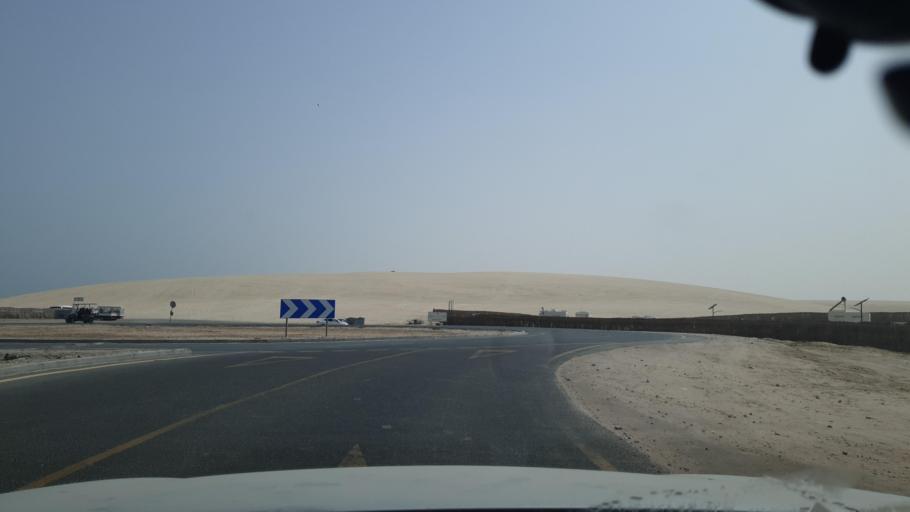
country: QA
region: Al Wakrah
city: Umm Sa'id
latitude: 24.8500
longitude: 51.5079
